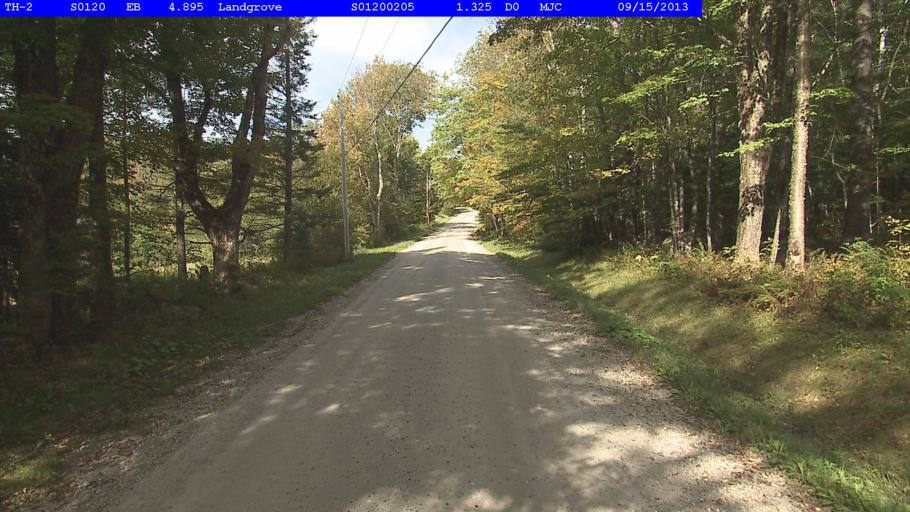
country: US
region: Vermont
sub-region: Bennington County
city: Manchester Center
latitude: 43.2783
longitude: -72.8592
